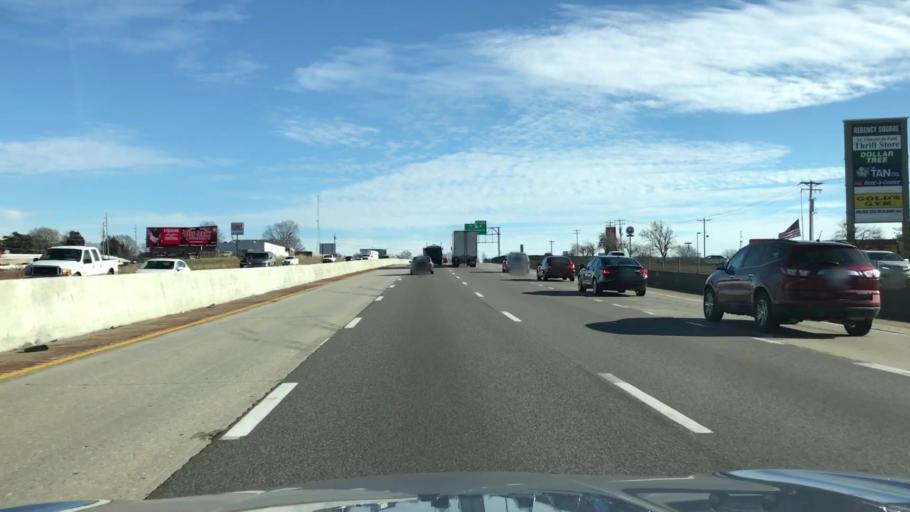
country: US
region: Missouri
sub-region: Saint Charles County
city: Saint Charles
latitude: 38.7855
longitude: -90.5284
